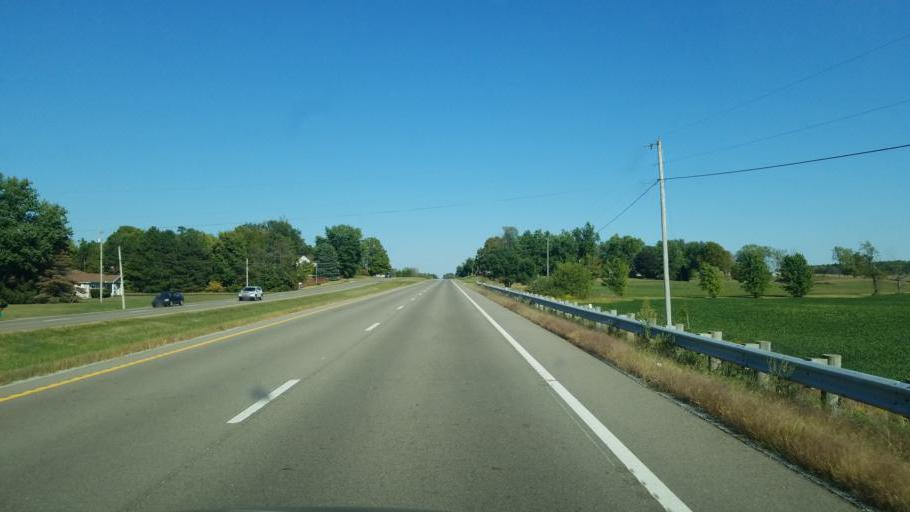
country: US
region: Ohio
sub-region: Clark County
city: Lisbon
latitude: 39.9287
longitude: -83.5850
